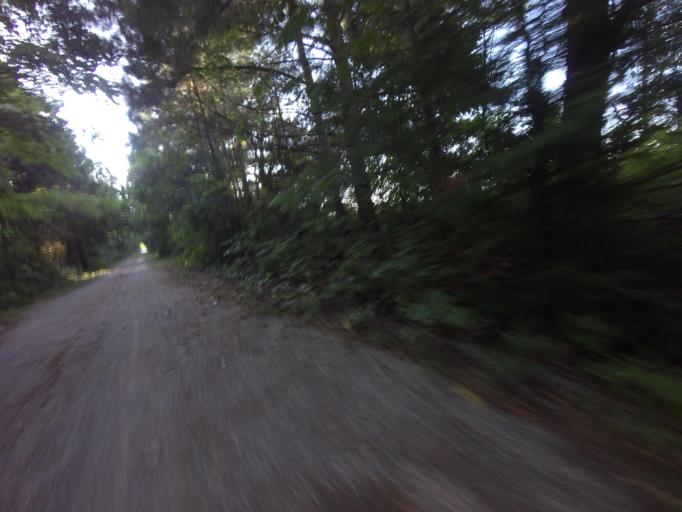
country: CA
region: Ontario
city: Goderich
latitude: 43.7534
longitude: -81.6687
